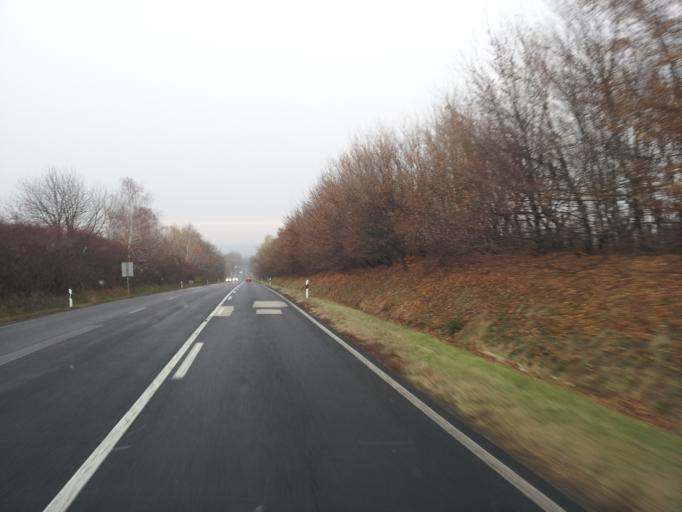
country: HU
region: Veszprem
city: Ajka
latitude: 47.1399
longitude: 17.5775
